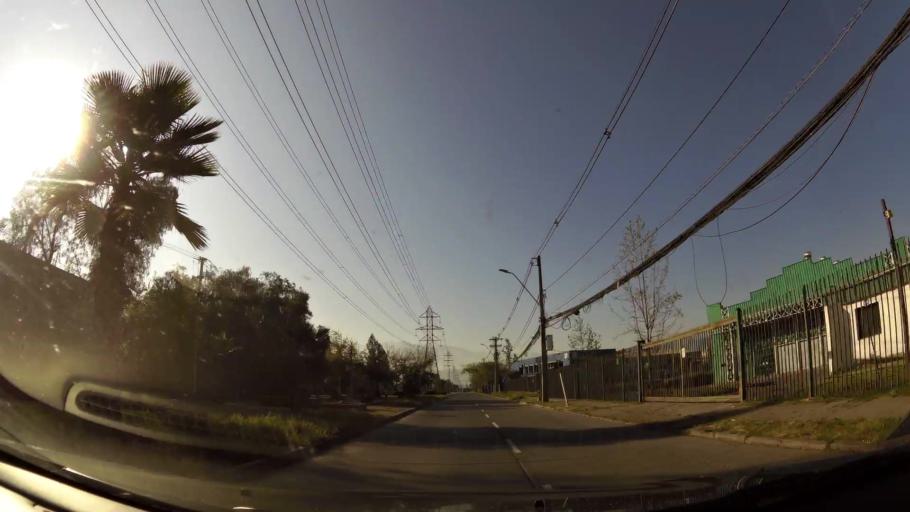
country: CL
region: Santiago Metropolitan
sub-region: Provincia de Santiago
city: Santiago
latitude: -33.3731
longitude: -70.6493
